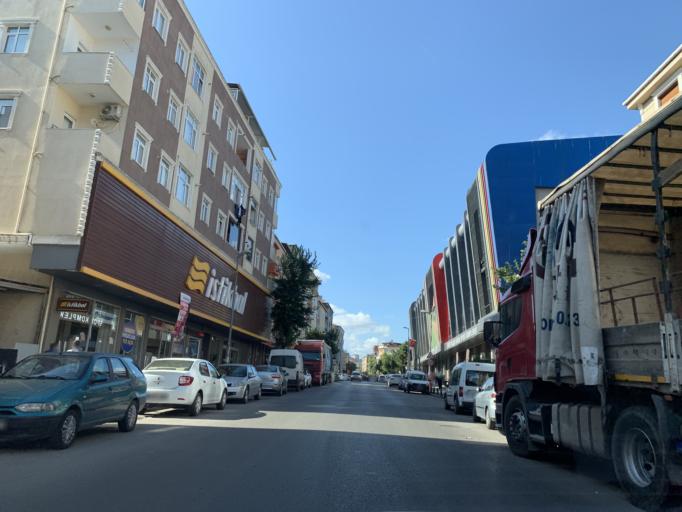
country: TR
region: Istanbul
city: Pendik
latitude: 40.8797
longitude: 29.2726
